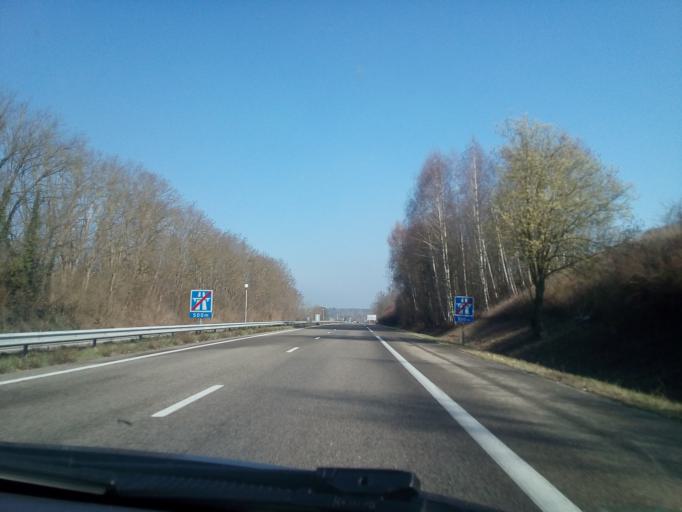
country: DE
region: Rheinland-Pfalz
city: Scheibenhardt
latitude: 48.9598
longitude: 8.1458
